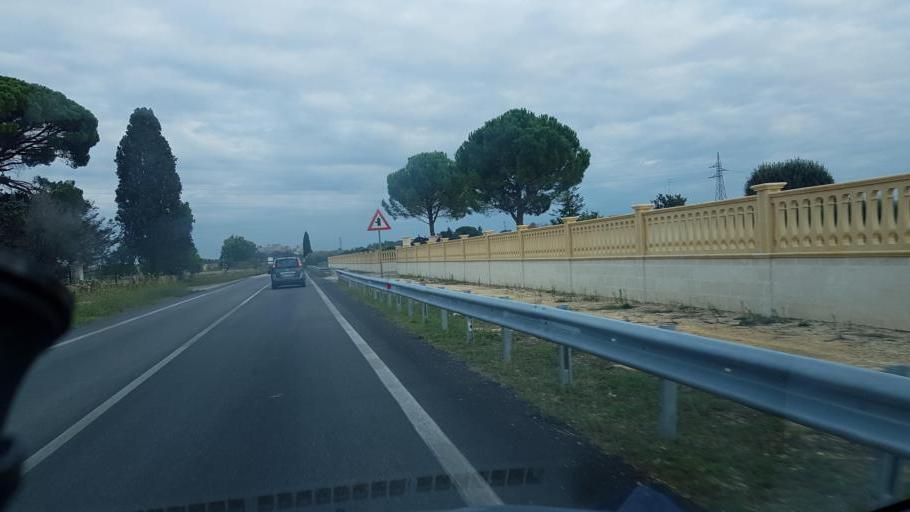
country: IT
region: Apulia
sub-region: Provincia di Brindisi
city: Oria
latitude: 40.5118
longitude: 17.6212
